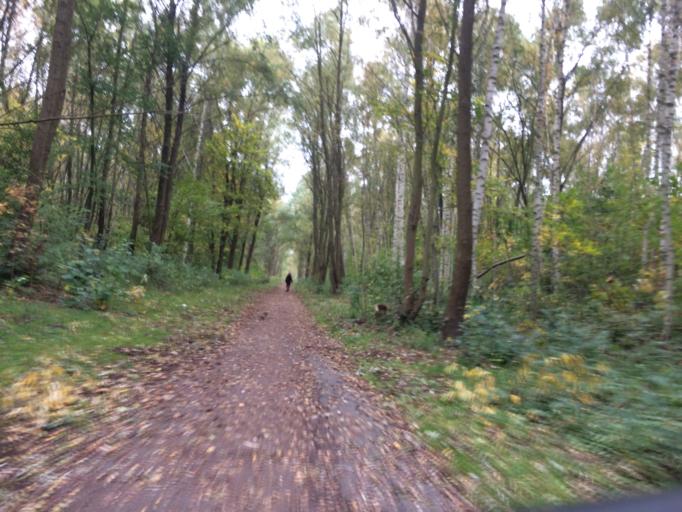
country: DE
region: Berlin
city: Rosenthal
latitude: 52.6006
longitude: 13.3722
